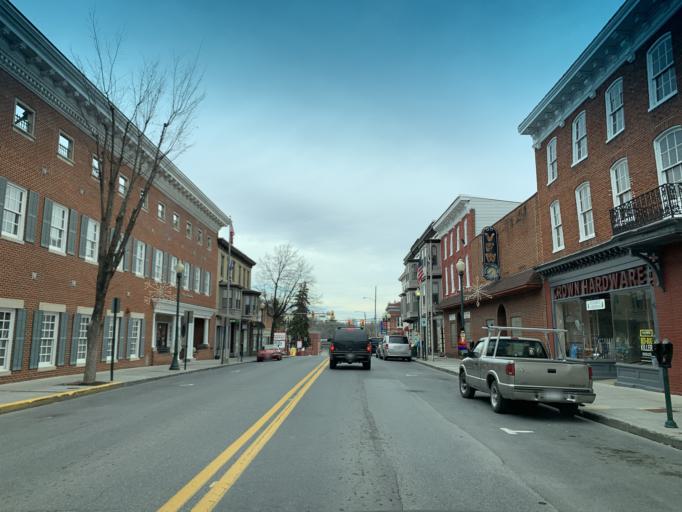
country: US
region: West Virginia
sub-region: Berkeley County
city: Martinsburg
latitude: 39.4592
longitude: -77.9630
